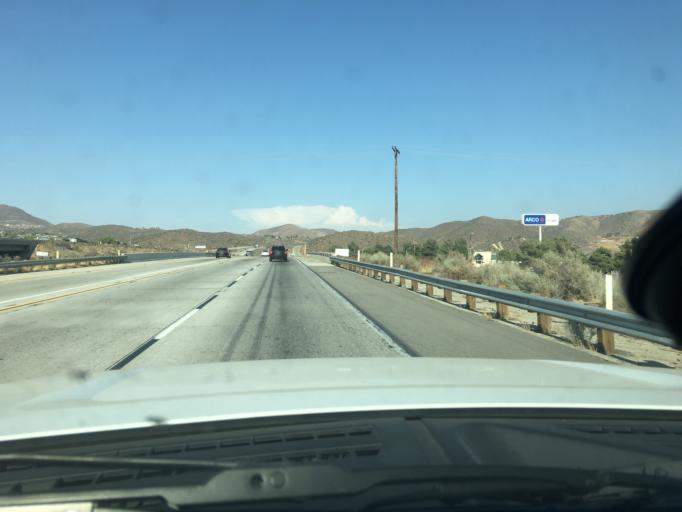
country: US
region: California
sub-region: Los Angeles County
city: Acton
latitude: 34.4911
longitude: -118.1997
